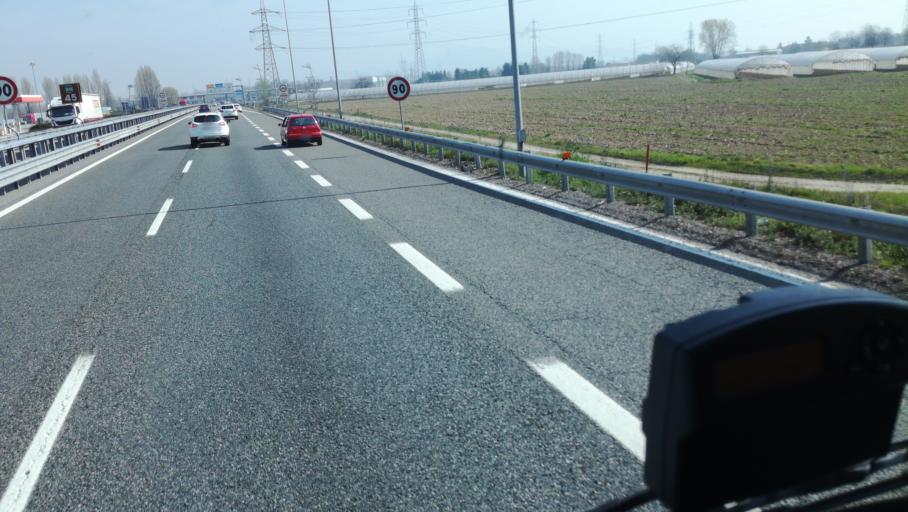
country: IT
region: Piedmont
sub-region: Provincia di Torino
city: Borgo Melano
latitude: 45.0111
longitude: 7.5800
